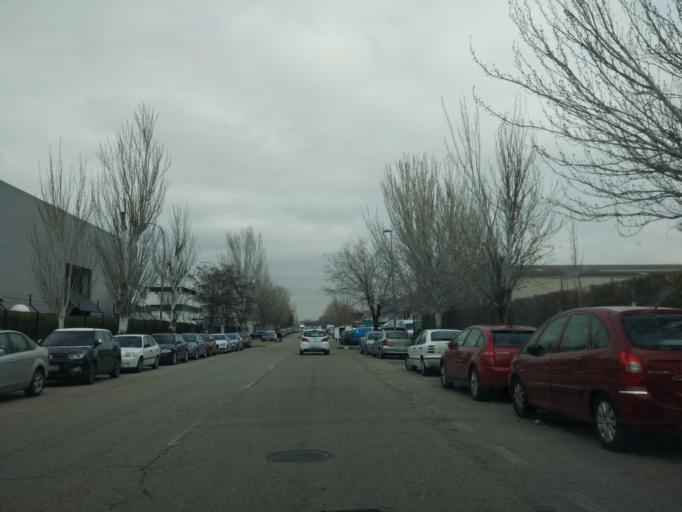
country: ES
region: Madrid
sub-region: Provincia de Madrid
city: Torrejon de Ardoz
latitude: 40.4577
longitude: -3.4977
